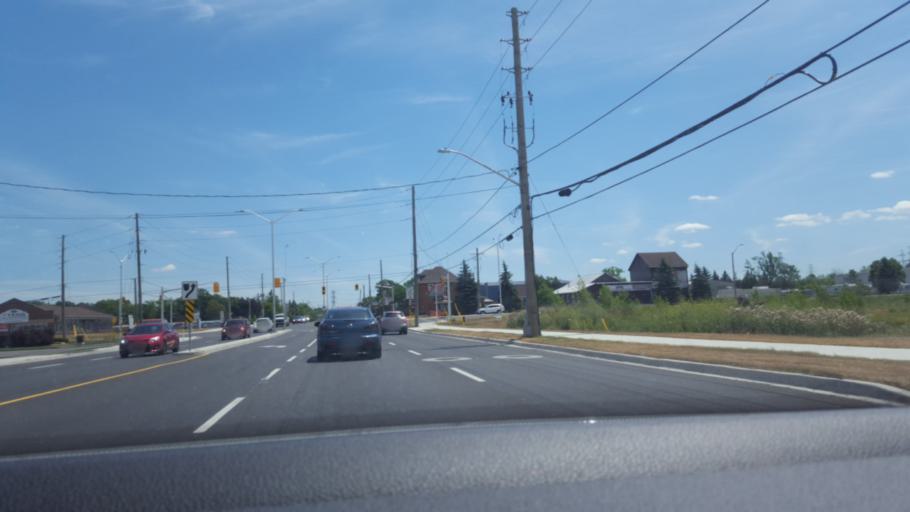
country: CA
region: Ontario
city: Hamilton
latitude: 43.1881
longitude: -79.8342
